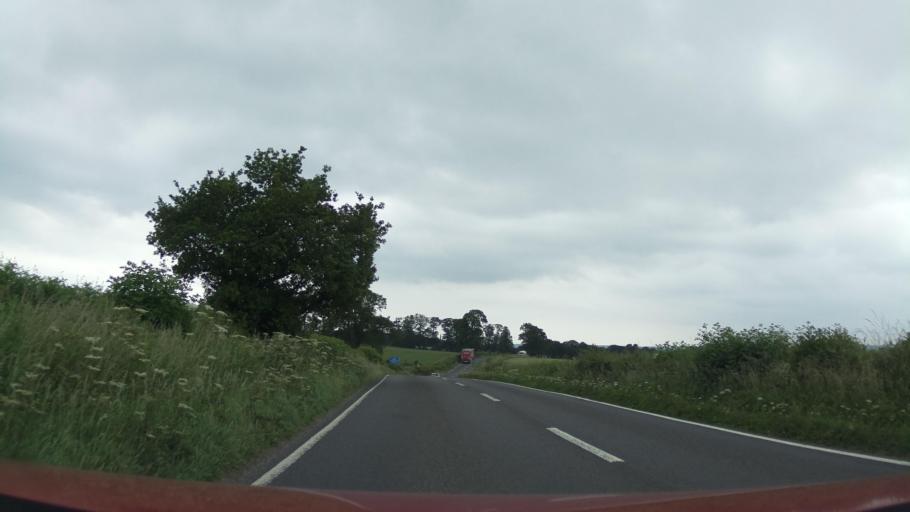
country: GB
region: England
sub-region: Derbyshire
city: Rodsley
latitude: 52.9156
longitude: -1.7605
